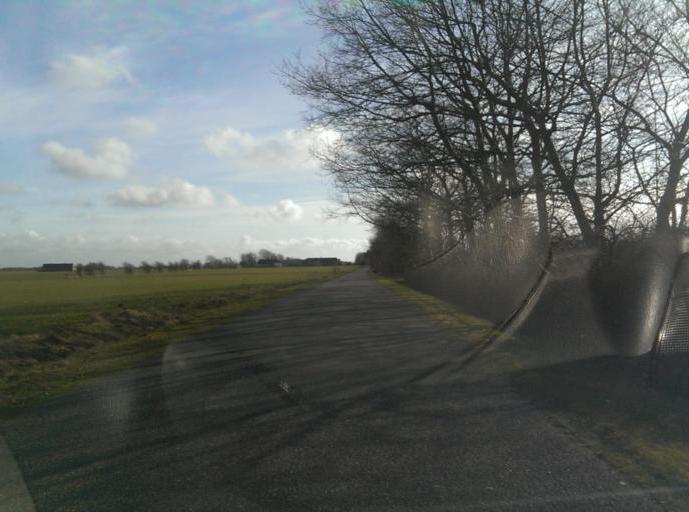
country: DK
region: South Denmark
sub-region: Esbjerg Kommune
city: Bramming
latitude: 55.4515
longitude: 8.7523
